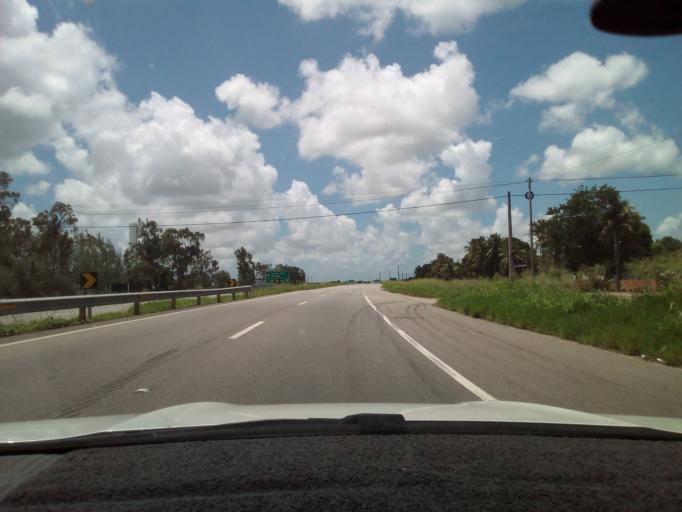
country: BR
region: Paraiba
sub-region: Santa Rita
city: Santa Rita
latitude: -7.1420
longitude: -34.9933
